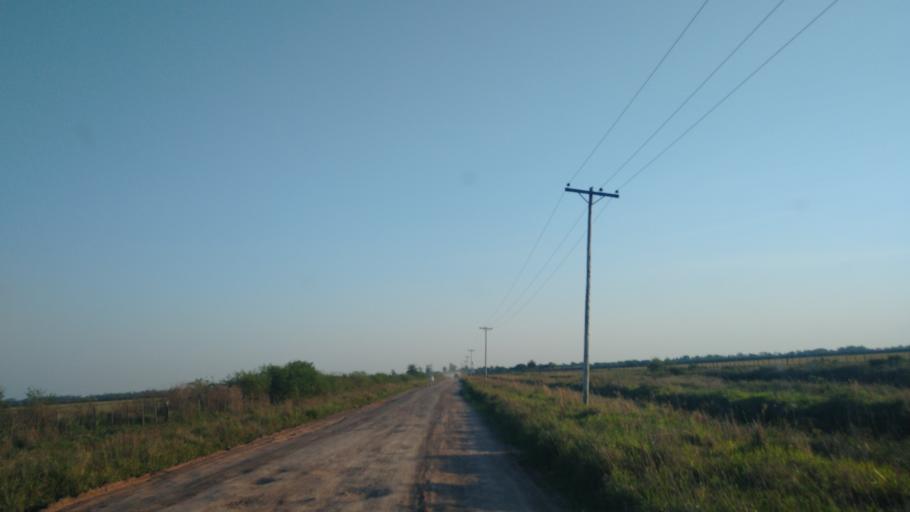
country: PY
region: Neembucu
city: Cerrito
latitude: -27.3862
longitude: -57.6575
